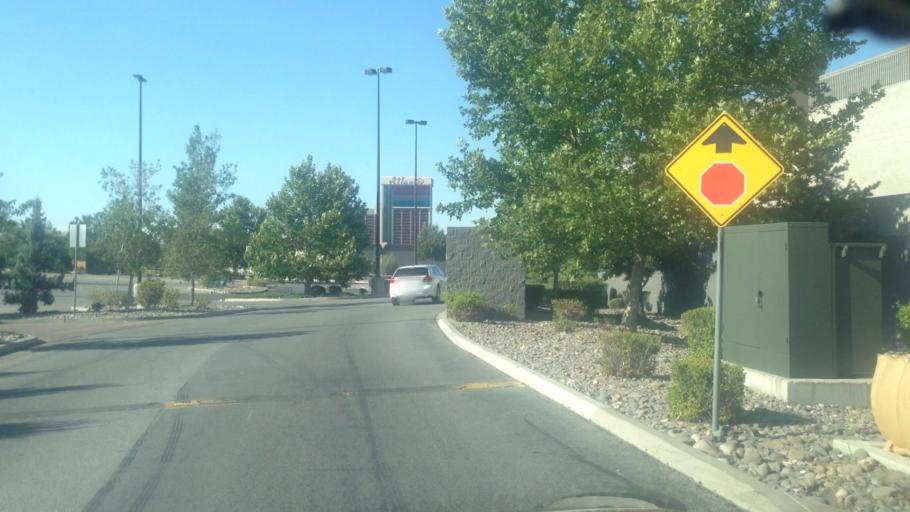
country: US
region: Nevada
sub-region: Washoe County
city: Reno
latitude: 39.4810
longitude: -119.7963
